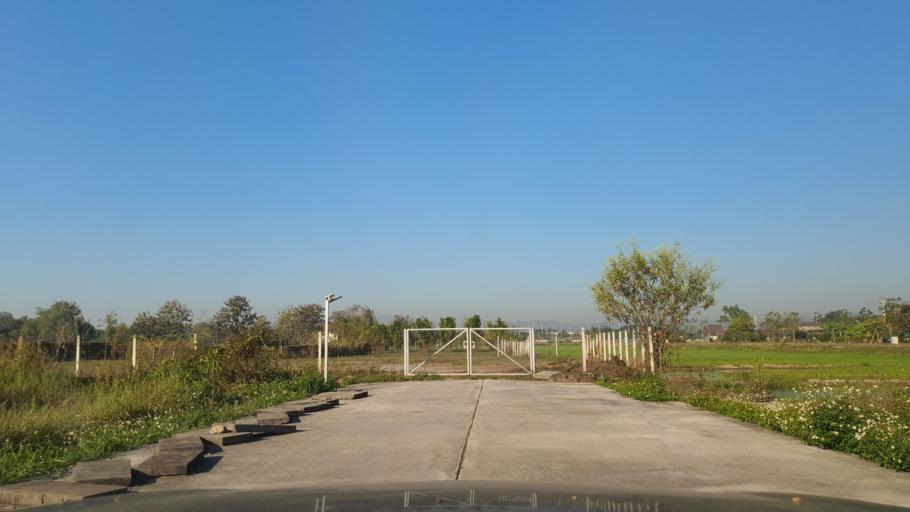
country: TH
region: Chiang Mai
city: Hang Dong
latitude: 18.6953
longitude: 98.9663
